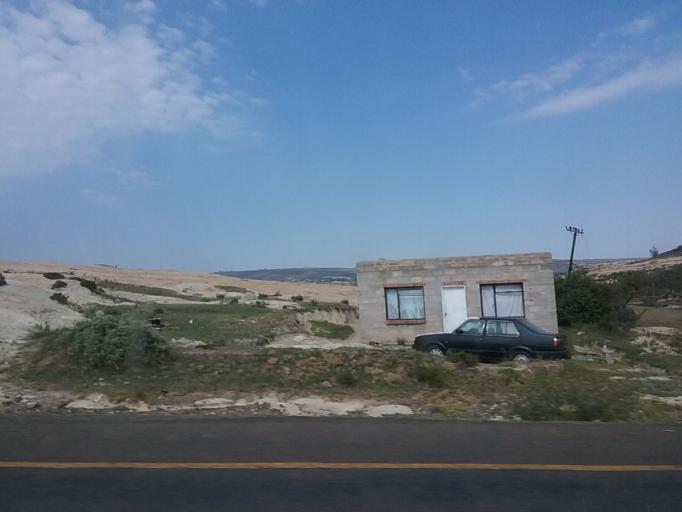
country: LS
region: Berea
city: Teyateyaneng
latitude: -29.1252
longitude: 27.9812
